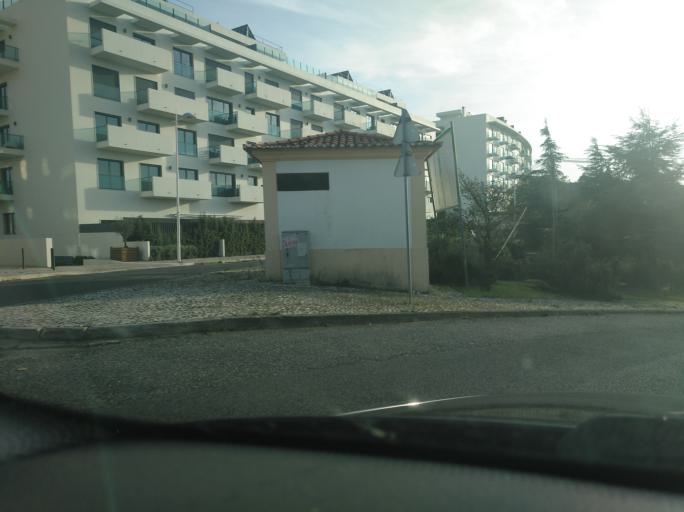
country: PT
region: Lisbon
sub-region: Odivelas
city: Olival do Basto
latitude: 38.7798
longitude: -9.1723
